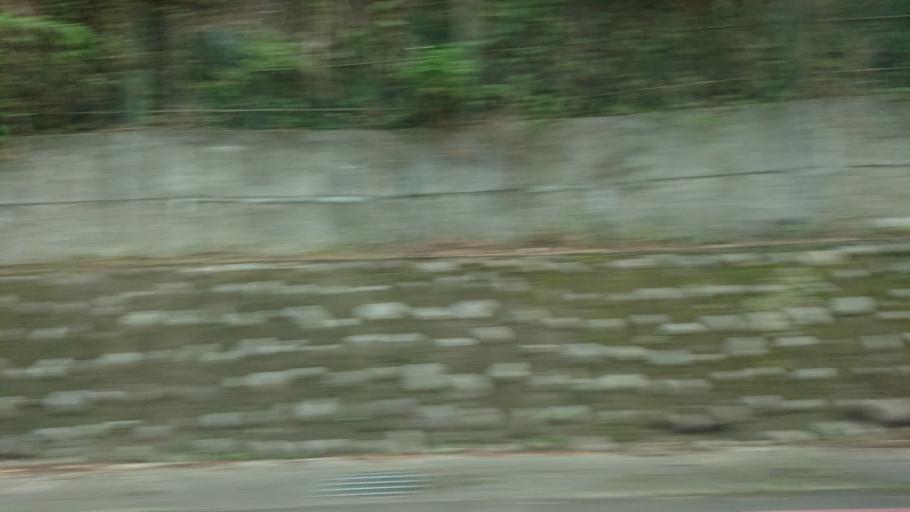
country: TW
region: Taiwan
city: Daxi
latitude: 24.8735
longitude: 121.4011
